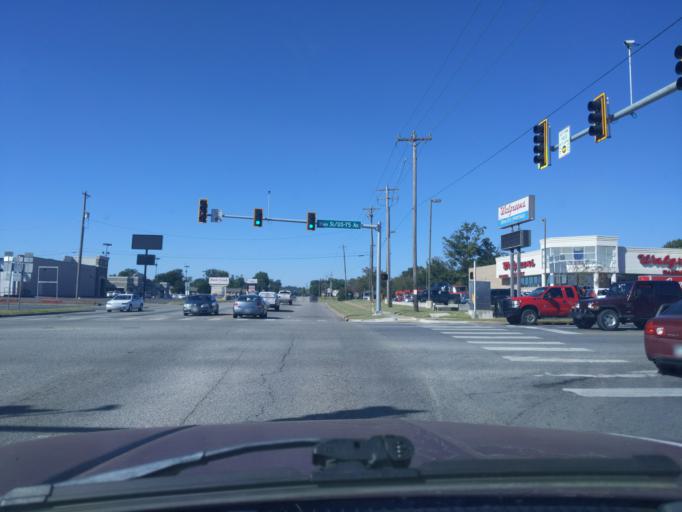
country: US
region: Oklahoma
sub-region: Creek County
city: Sapulpa
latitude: 35.9885
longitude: -96.1135
